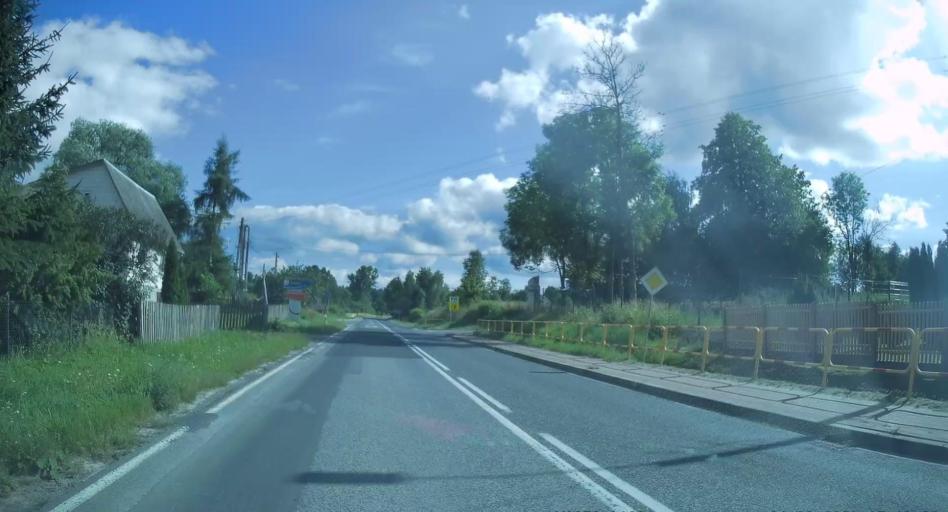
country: PL
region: Swietokrzyskie
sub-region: Powiat kielecki
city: Nowa Slupia
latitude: 50.8221
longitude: 21.0767
